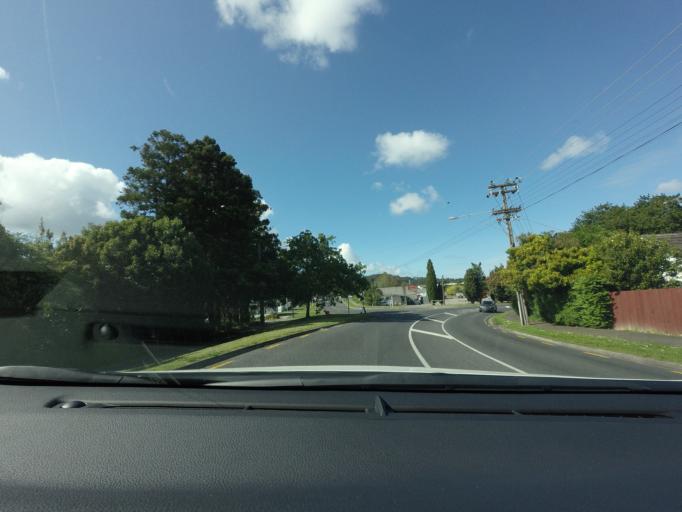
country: NZ
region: Auckland
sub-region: Auckland
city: Rosebank
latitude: -36.7553
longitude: 174.5917
